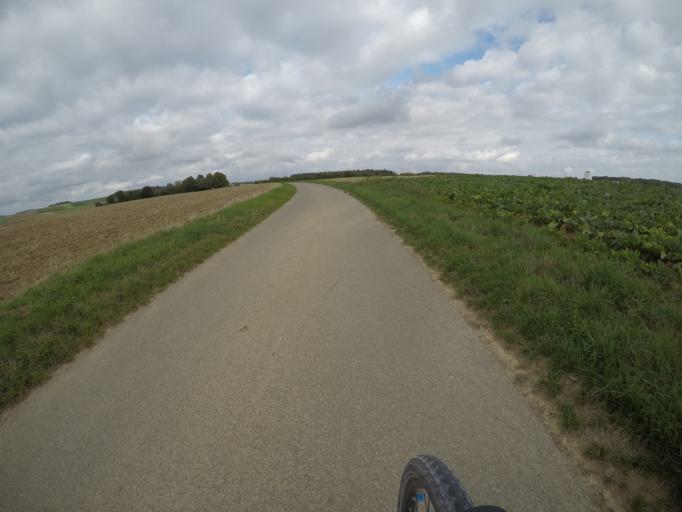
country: DE
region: Baden-Wuerttemberg
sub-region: Regierungsbezirk Stuttgart
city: Renningen
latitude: 48.7389
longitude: 8.9253
